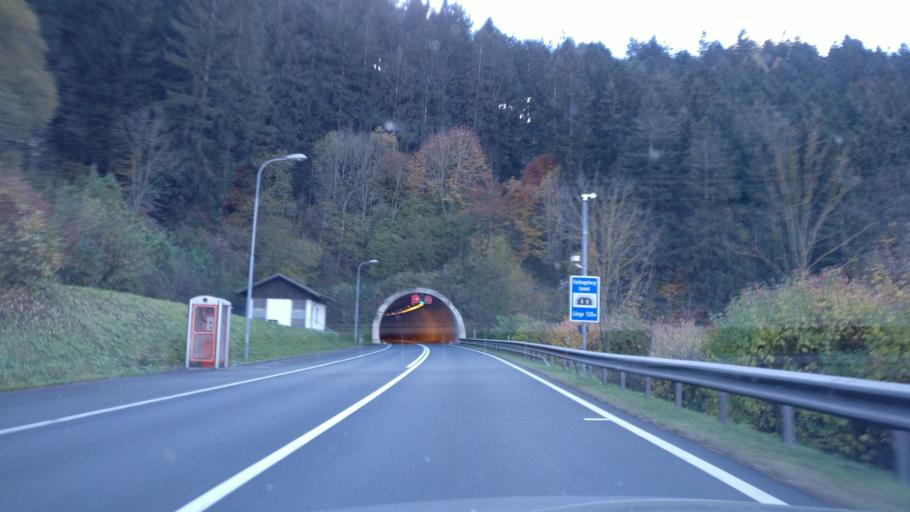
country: AT
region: Carinthia
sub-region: Politischer Bezirk Spittal an der Drau
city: Sachsenburg
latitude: 46.8261
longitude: 13.3580
